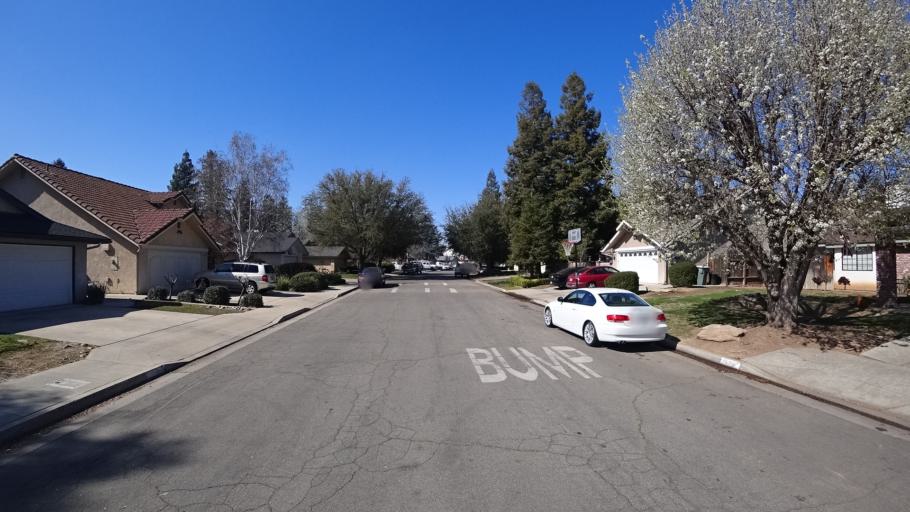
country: US
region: California
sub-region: Fresno County
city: Clovis
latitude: 36.8712
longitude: -119.7532
